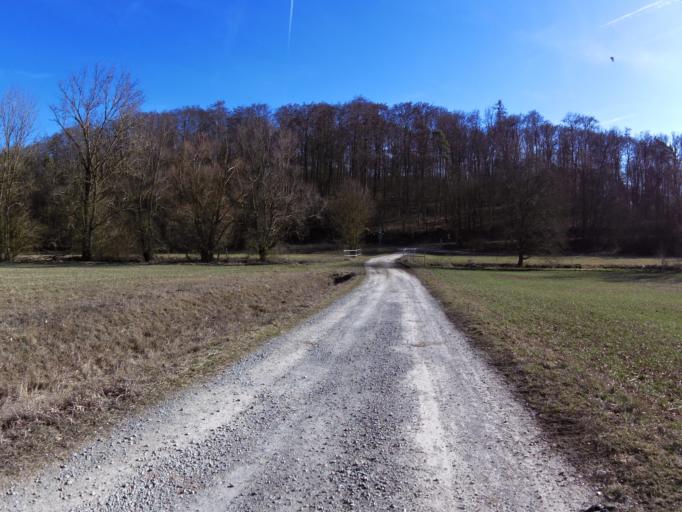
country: DE
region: Bavaria
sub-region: Regierungsbezirk Unterfranken
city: Rimpar
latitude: 49.8573
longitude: 9.9830
